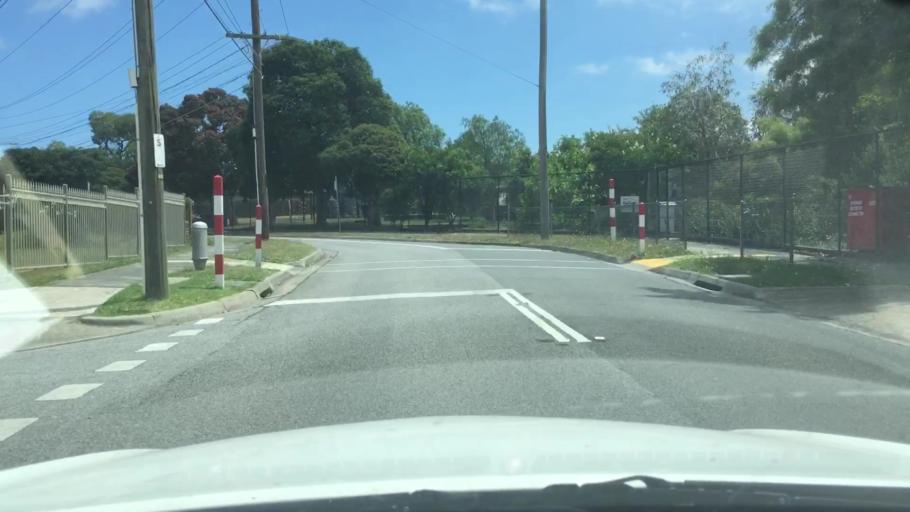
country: AU
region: Victoria
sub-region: Greater Dandenong
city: Keysborough
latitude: -37.9926
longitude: 145.1805
